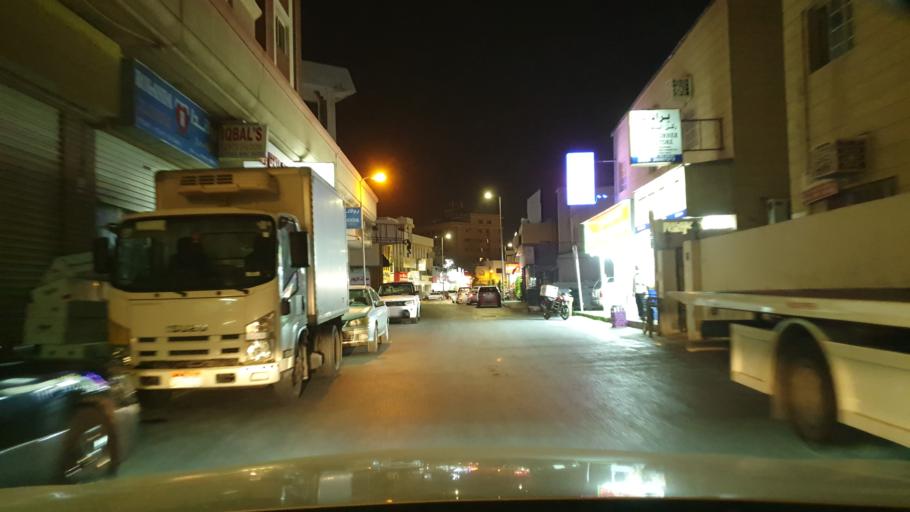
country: BH
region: Manama
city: Manama
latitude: 26.2142
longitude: 50.5864
